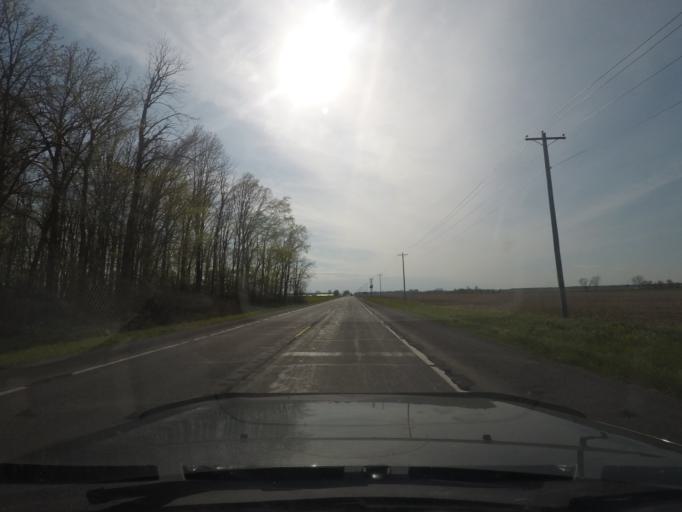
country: US
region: Michigan
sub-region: Berrien County
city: Three Oaks
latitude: 41.7982
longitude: -86.5380
